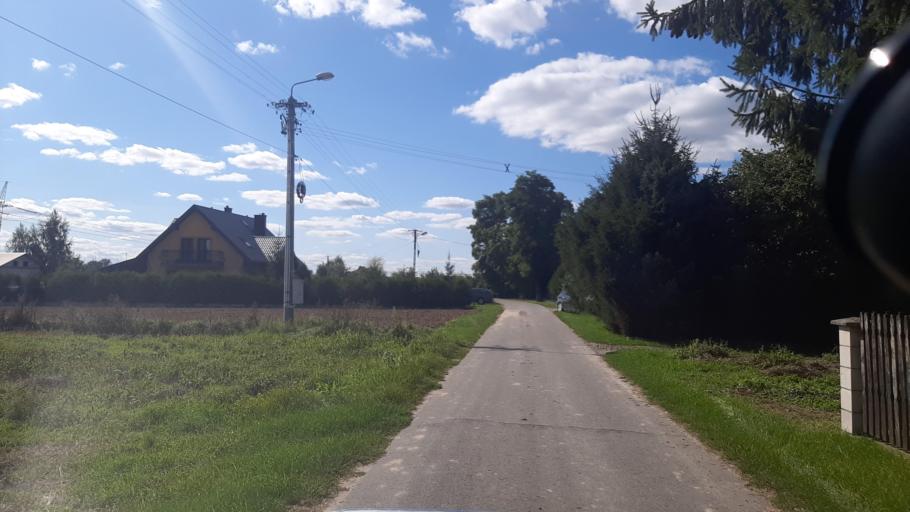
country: PL
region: Lublin Voivodeship
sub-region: Powiat pulawski
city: Markuszow
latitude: 51.3967
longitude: 22.2326
